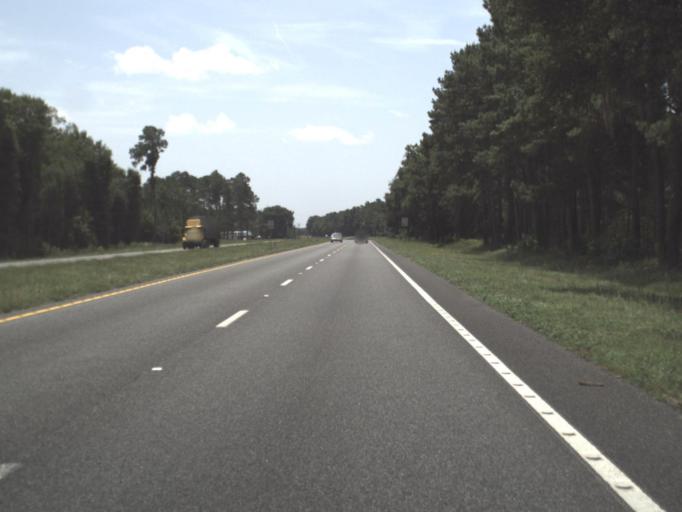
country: US
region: Florida
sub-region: Taylor County
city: Perry
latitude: 29.9884
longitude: -83.4969
